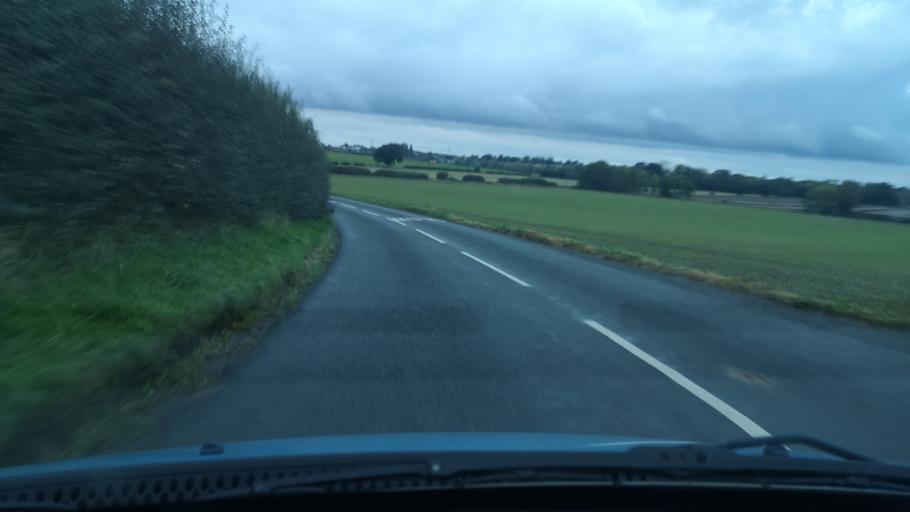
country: GB
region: England
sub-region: Doncaster
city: Norton
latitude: 53.6344
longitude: -1.2022
